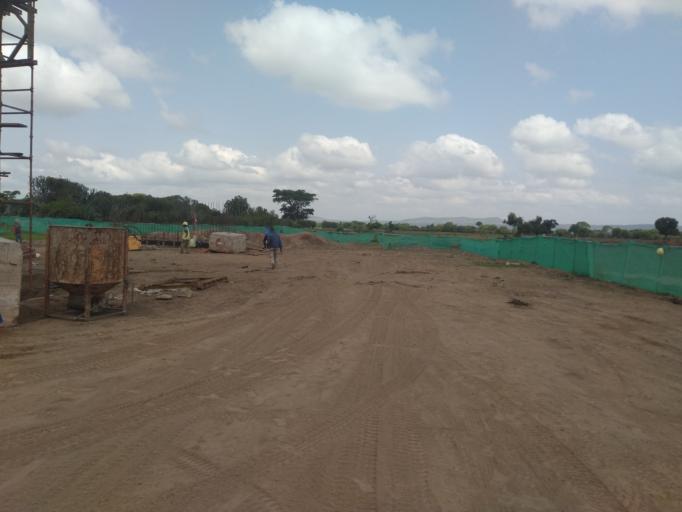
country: ET
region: Oromiya
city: Shashemene
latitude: 7.3547
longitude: 38.6396
